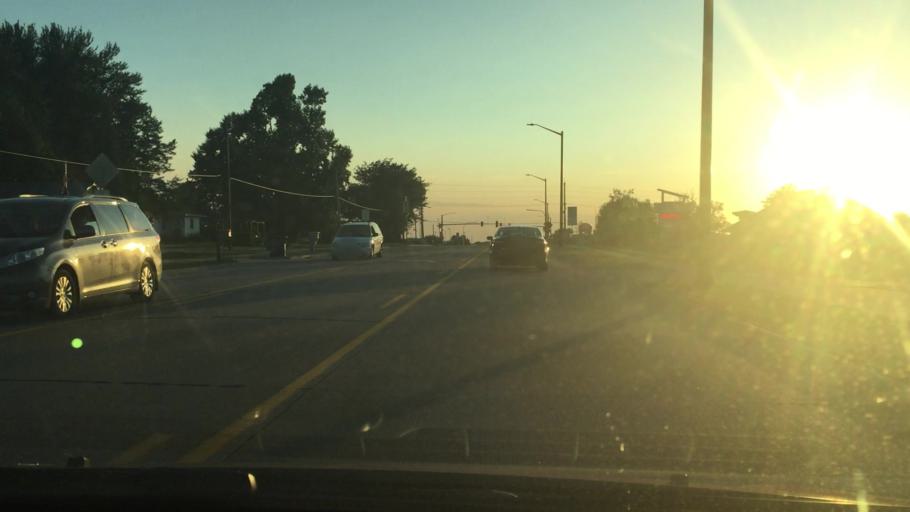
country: US
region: Iowa
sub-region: Muscatine County
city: Muscatine
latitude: 41.4360
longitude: -91.0764
